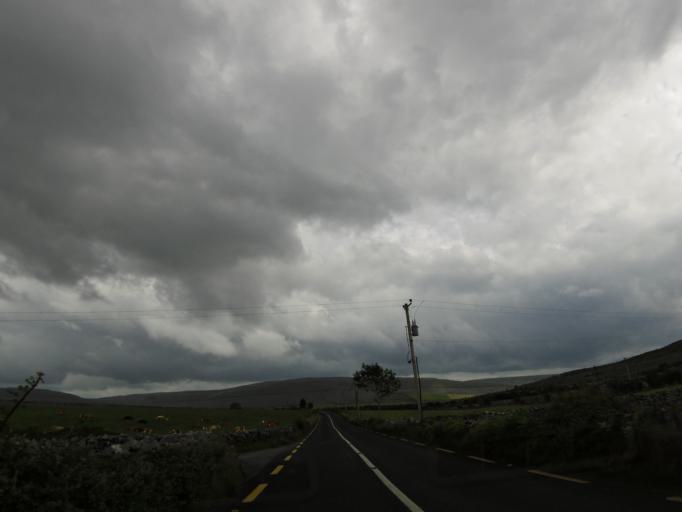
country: IE
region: Connaught
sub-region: County Galway
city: Bearna
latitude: 53.1269
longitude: -9.0906
